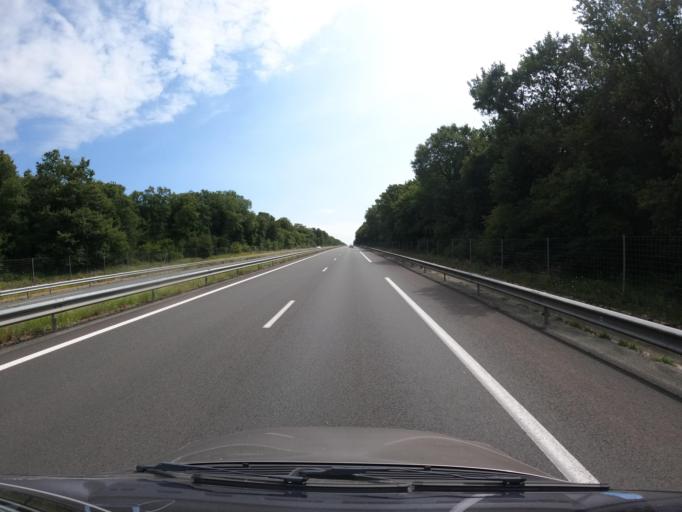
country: FR
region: Poitou-Charentes
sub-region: Departement de la Charente-Maritime
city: Courcon
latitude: 46.2203
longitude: -0.8017
